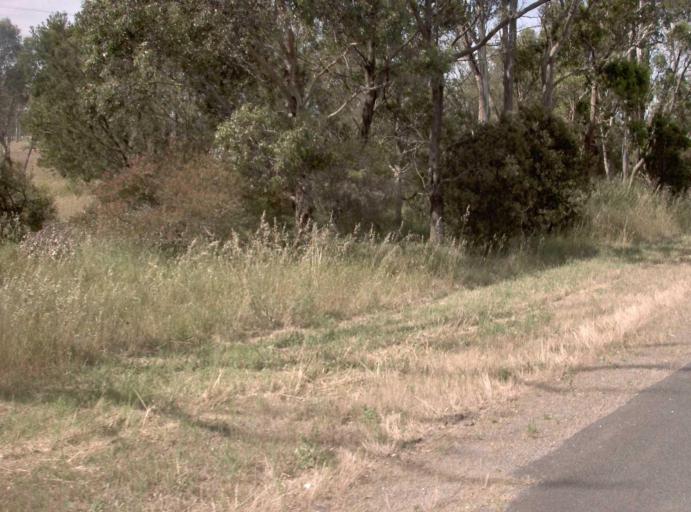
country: AU
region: Victoria
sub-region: East Gippsland
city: Bairnsdale
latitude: -37.8595
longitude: 147.5207
